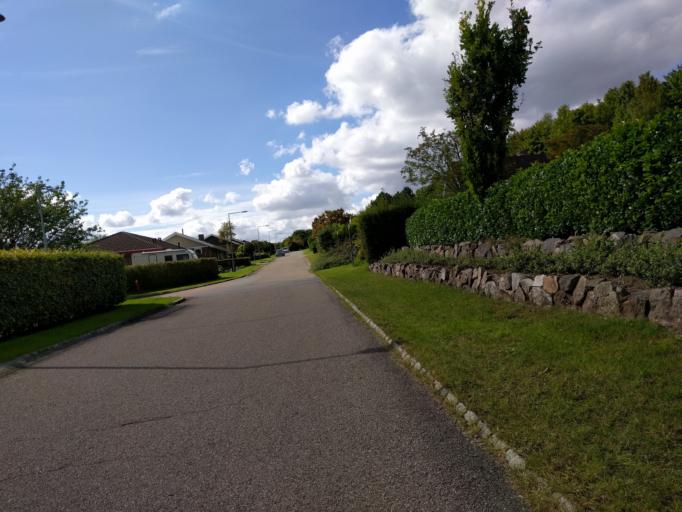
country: DK
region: South Denmark
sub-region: Kerteminde Kommune
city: Munkebo
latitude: 55.4670
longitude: 10.5774
